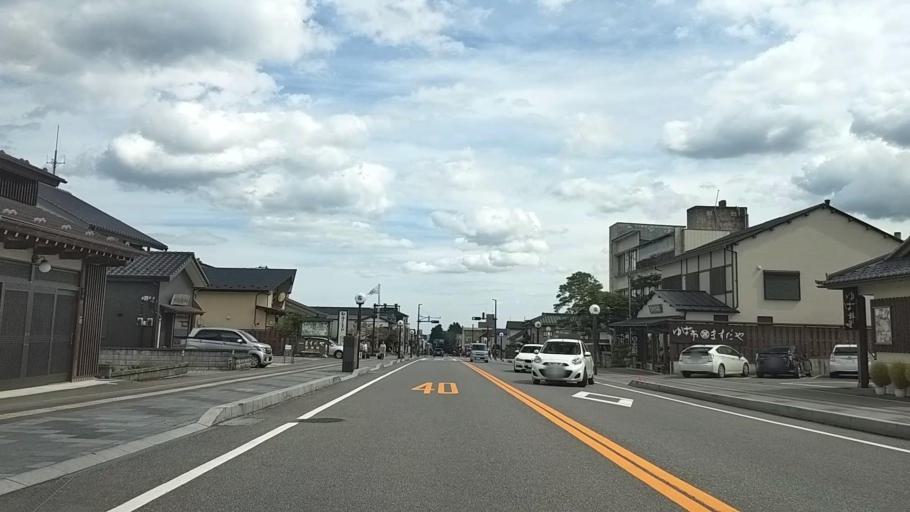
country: JP
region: Tochigi
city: Nikko
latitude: 36.7490
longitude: 139.6144
